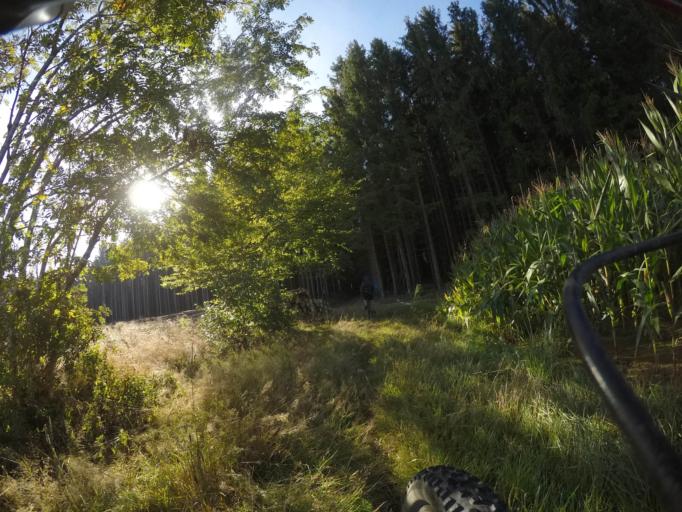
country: BE
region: Wallonia
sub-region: Province du Luxembourg
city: Fauvillers
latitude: 49.9028
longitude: 5.6662
